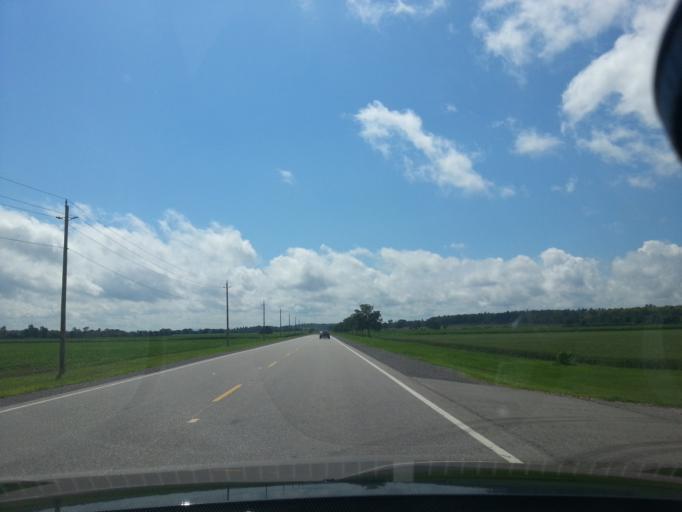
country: CA
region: Ontario
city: Renfrew
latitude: 45.5217
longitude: -76.9008
